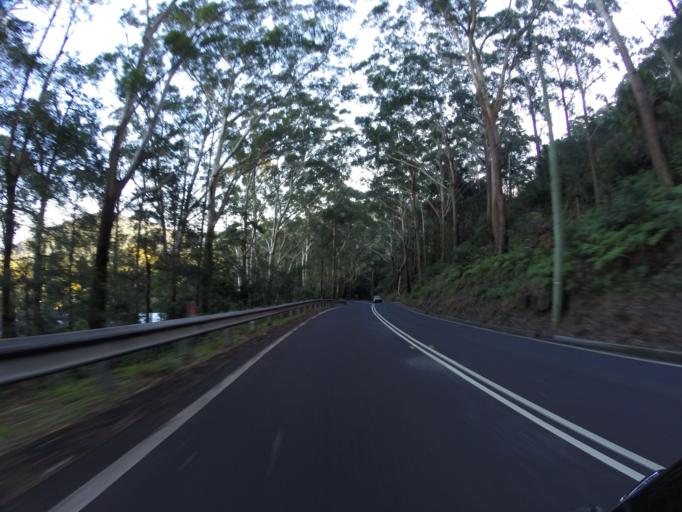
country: AU
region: New South Wales
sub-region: Wollongong
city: Helensburgh
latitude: -34.2235
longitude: 150.9876
